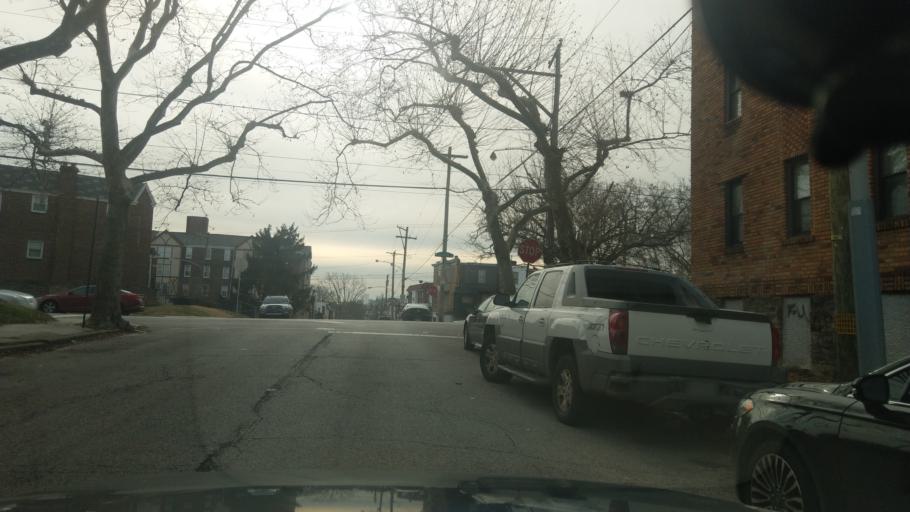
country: US
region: Pennsylvania
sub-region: Montgomery County
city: Wyncote
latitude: 40.0466
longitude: -75.1480
